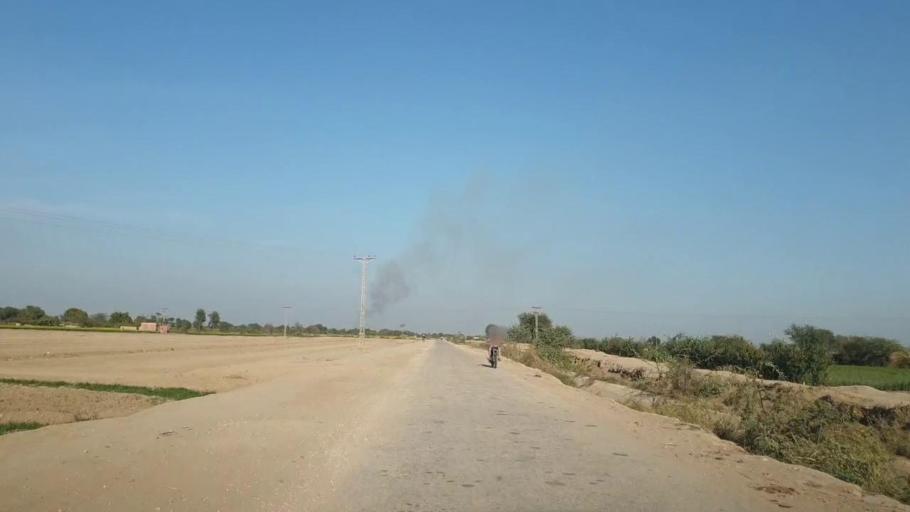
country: PK
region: Sindh
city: Tando Adam
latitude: 25.6952
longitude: 68.6820
